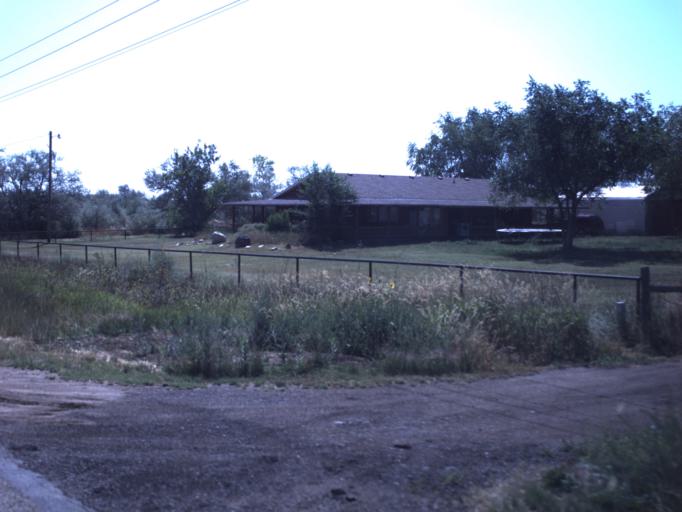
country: US
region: Utah
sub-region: Duchesne County
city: Roosevelt
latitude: 40.2581
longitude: -110.1339
